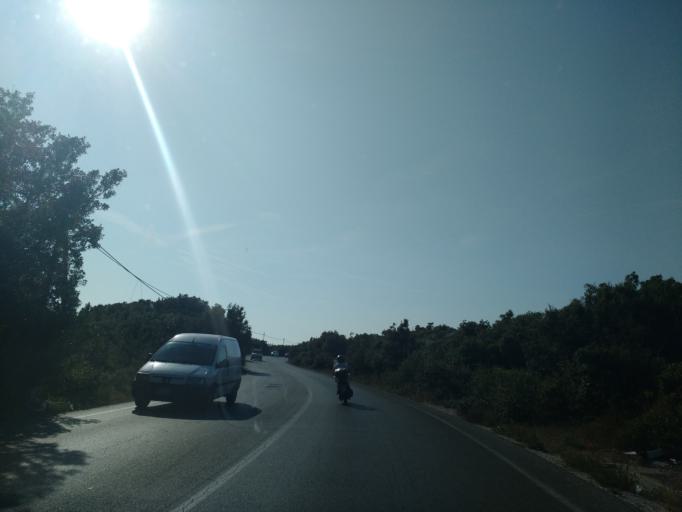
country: IT
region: Latium
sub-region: Citta metropolitana di Roma Capitale
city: Acilia-Castel Fusano-Ostia Antica
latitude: 41.6995
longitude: 12.3542
